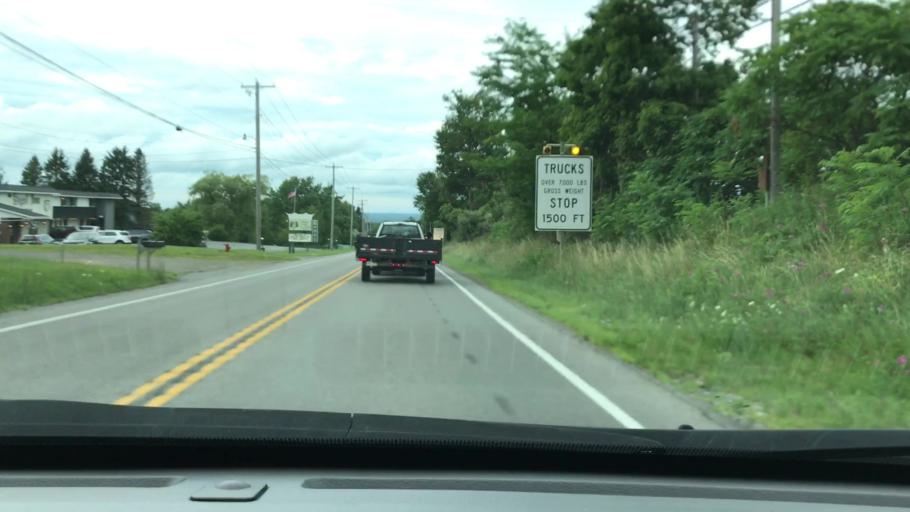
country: US
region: Pennsylvania
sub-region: Elk County
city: Ridgway
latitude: 41.4052
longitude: -78.7056
